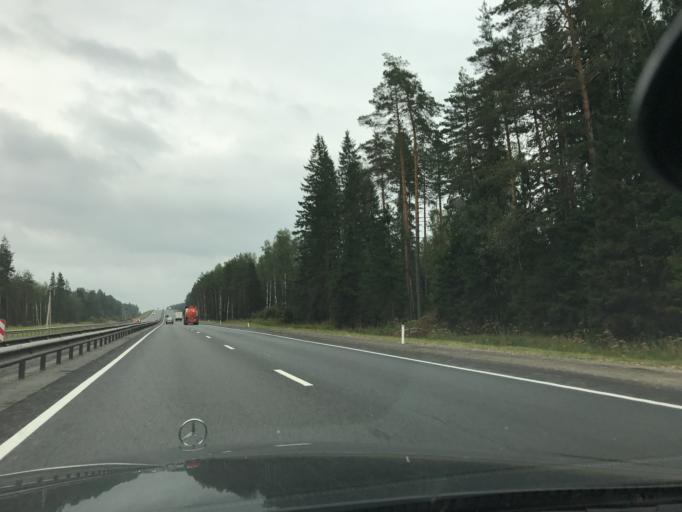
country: RU
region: Vladimir
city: Krasnyy Oktyabr'
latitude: 56.2171
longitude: 41.4315
